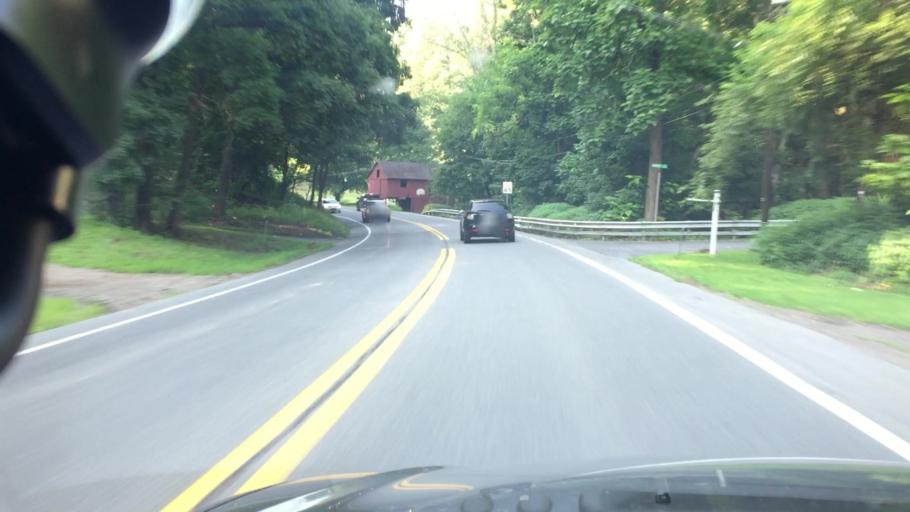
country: US
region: Pennsylvania
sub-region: Columbia County
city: Catawissa
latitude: 40.9333
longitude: -76.4574
